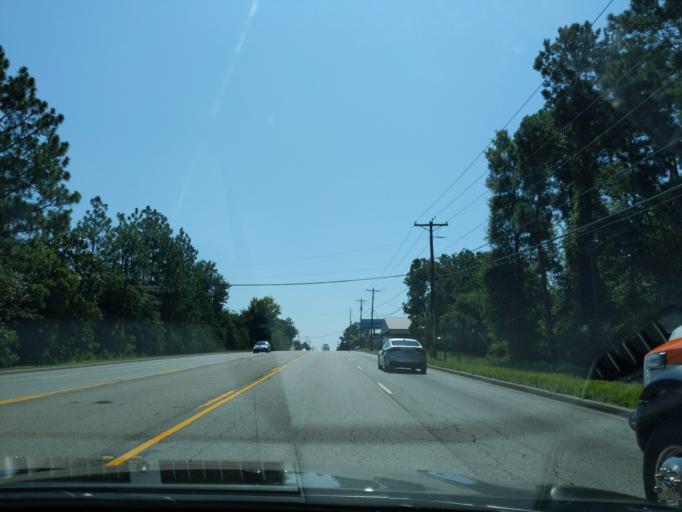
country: US
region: South Carolina
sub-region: Lexington County
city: Oak Grove
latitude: 33.9766
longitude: -81.1840
